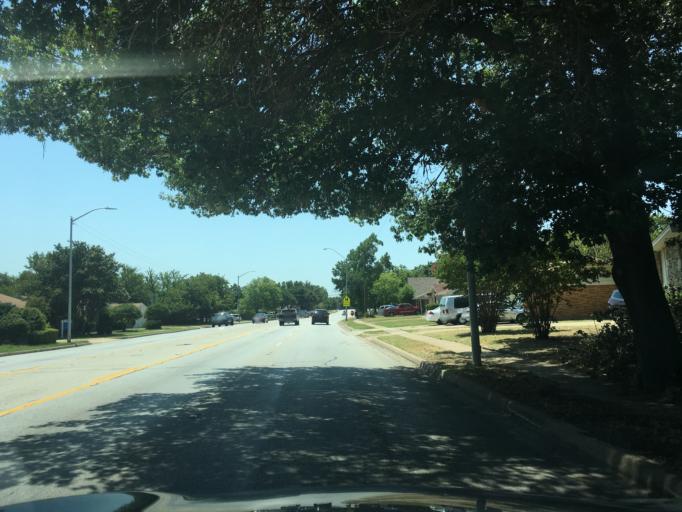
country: US
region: Texas
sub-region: Tarrant County
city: Edgecliff Village
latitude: 32.6610
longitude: -97.3566
